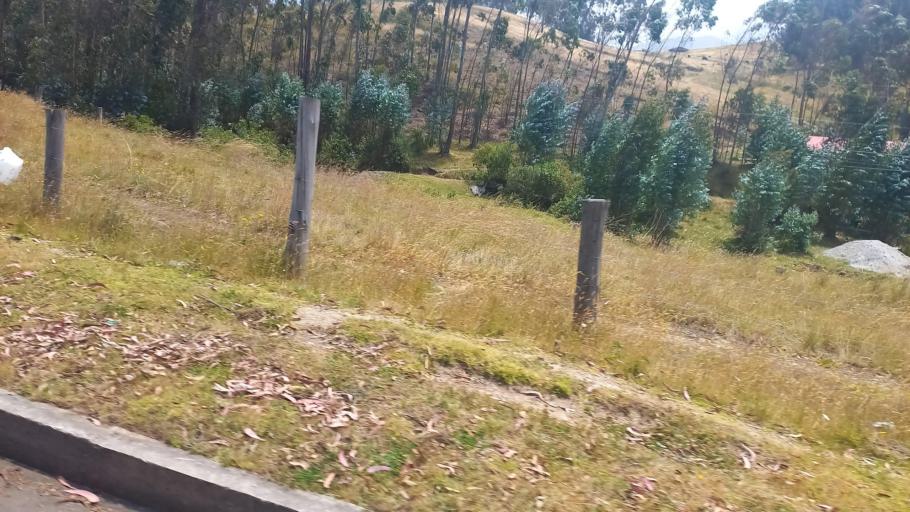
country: EC
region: Pichincha
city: Cayambe
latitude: 0.1761
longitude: -78.0906
